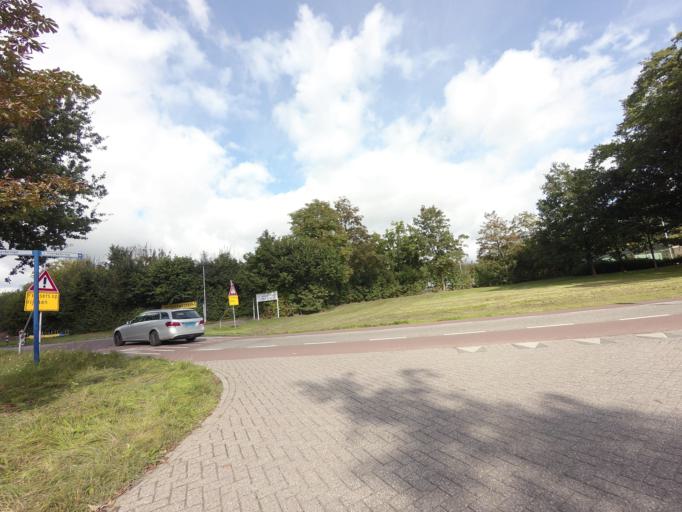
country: NL
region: Overijssel
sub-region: Gemeente Olst-Wijhe
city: Boskamp
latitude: 52.3321
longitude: 6.1229
